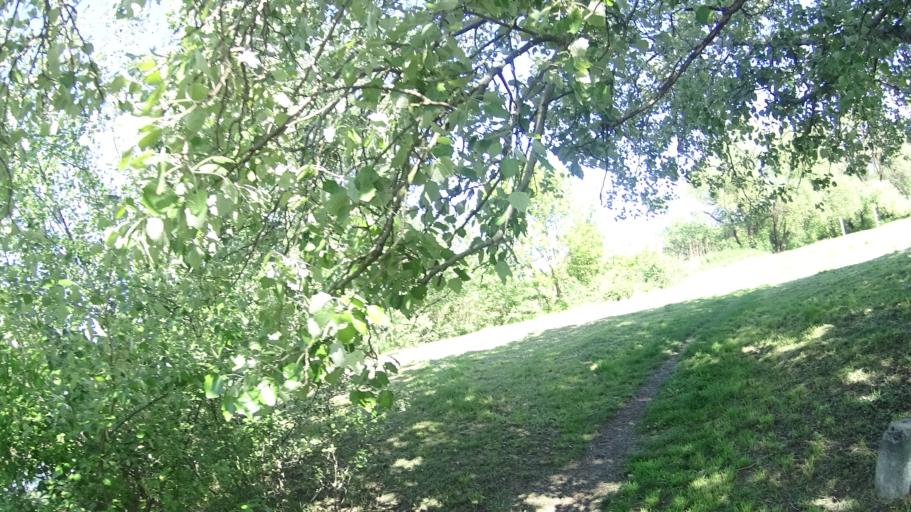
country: HU
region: Budapest
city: Budapest XXIII. keruelet
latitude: 47.3948
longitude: 19.1110
